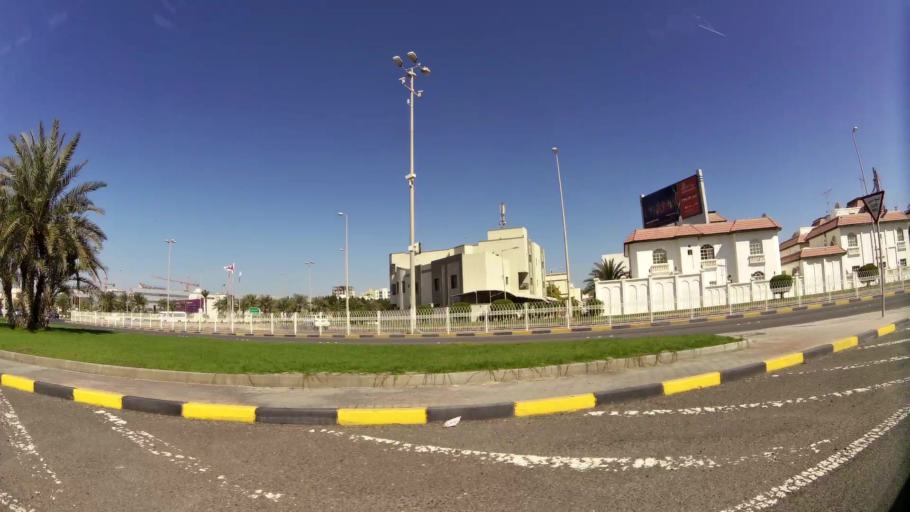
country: BH
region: Muharraq
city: Al Muharraq
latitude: 26.2605
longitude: 50.6041
